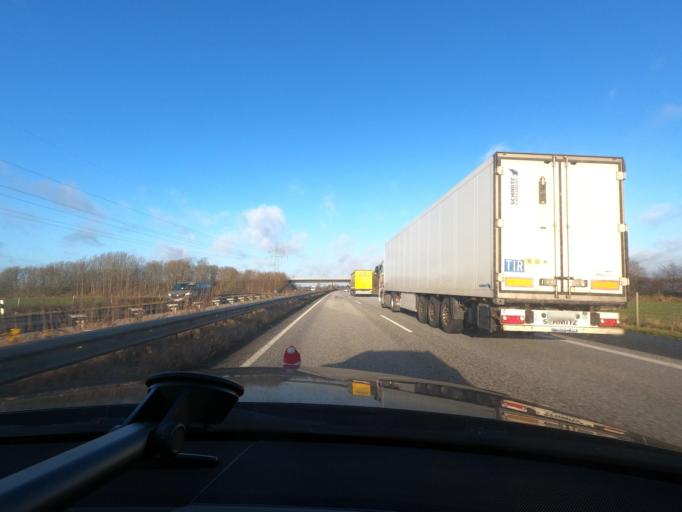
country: DE
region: Schleswig-Holstein
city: Lurschau
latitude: 54.5526
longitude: 9.4673
